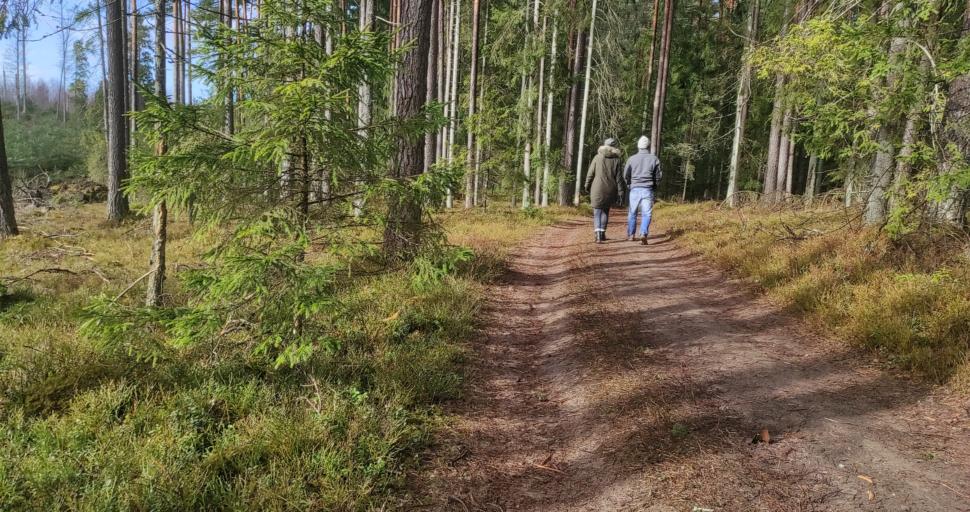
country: LV
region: Tukuma Rajons
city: Tukums
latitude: 57.1126
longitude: 23.0429
